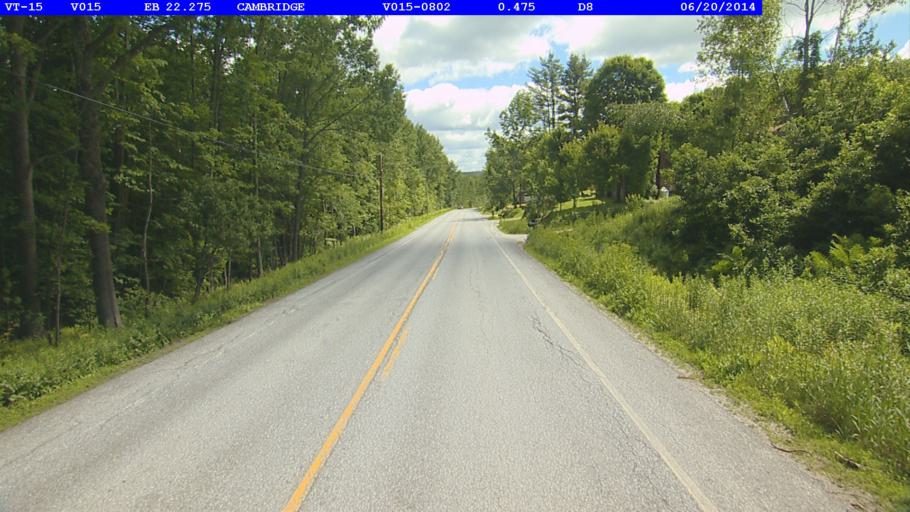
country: US
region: Vermont
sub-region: Chittenden County
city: Jericho
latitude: 44.6367
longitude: -72.9096
